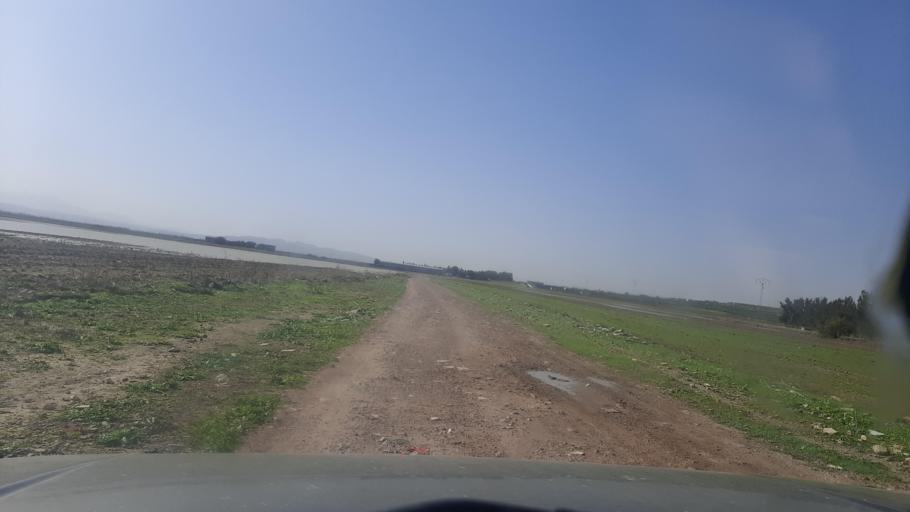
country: TN
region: Tunis
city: La Mohammedia
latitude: 36.6514
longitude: 10.0883
